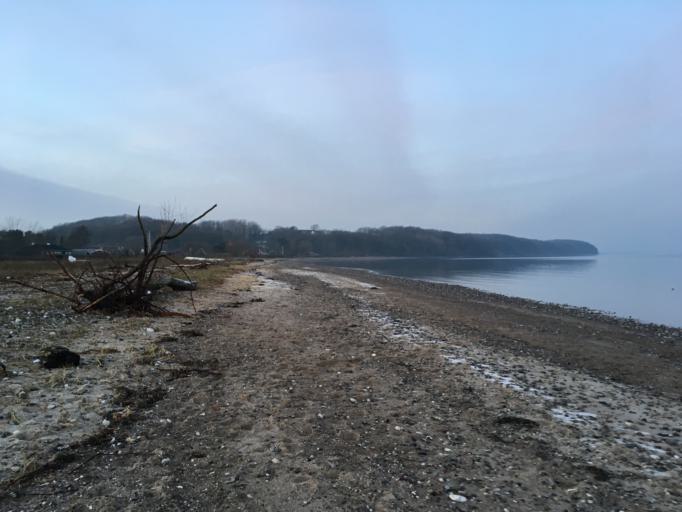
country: DK
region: South Denmark
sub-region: Middelfart Kommune
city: Norre Aby
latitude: 55.5215
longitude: 9.8525
